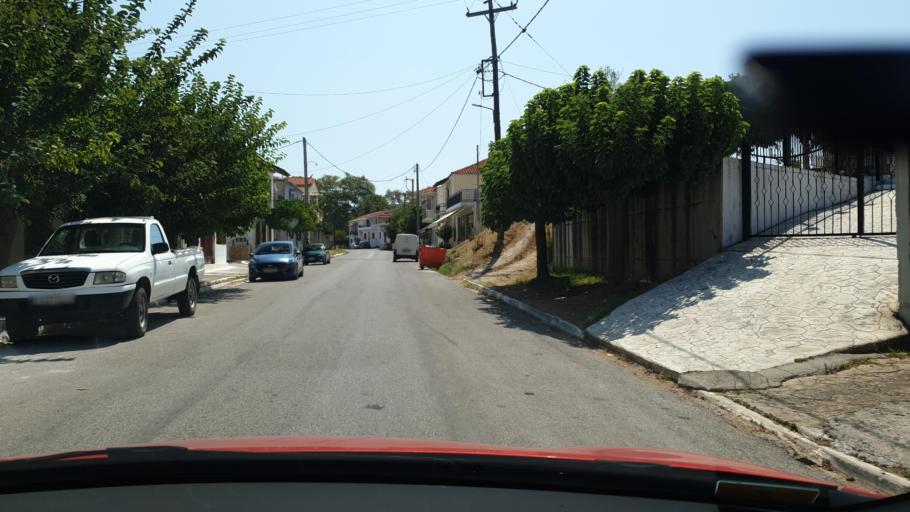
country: GR
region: Central Greece
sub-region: Nomos Evvoias
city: Oxilithos
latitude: 38.5437
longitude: 24.0750
